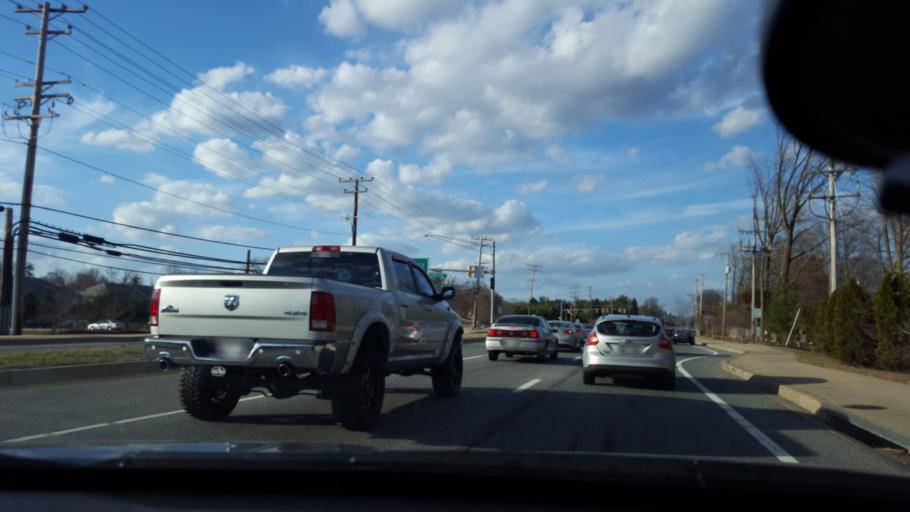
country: US
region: Maryland
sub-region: Prince George's County
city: Bowie
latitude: 38.9720
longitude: -76.7556
